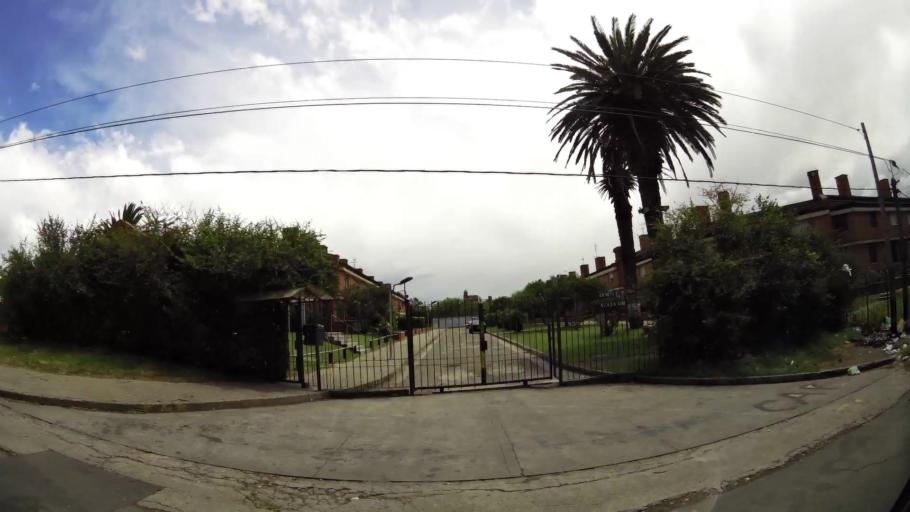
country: UY
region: Montevideo
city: Montevideo
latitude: -34.8774
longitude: -56.1315
